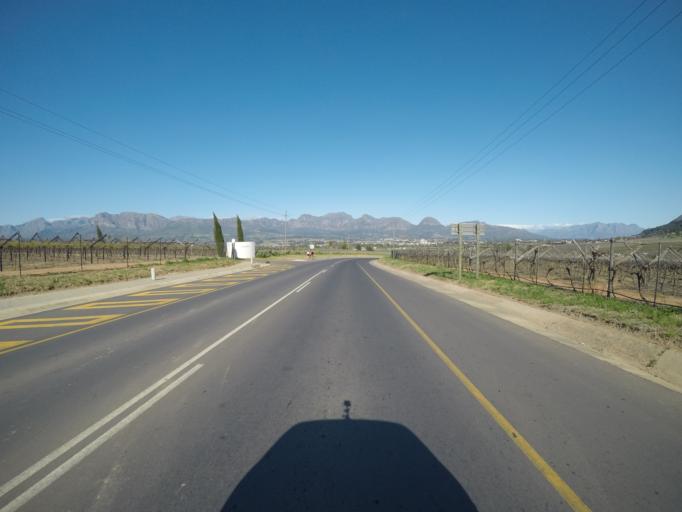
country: ZA
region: Western Cape
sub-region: Cape Winelands District Municipality
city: Noorder-Paarl
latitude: -33.6924
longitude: 18.9560
